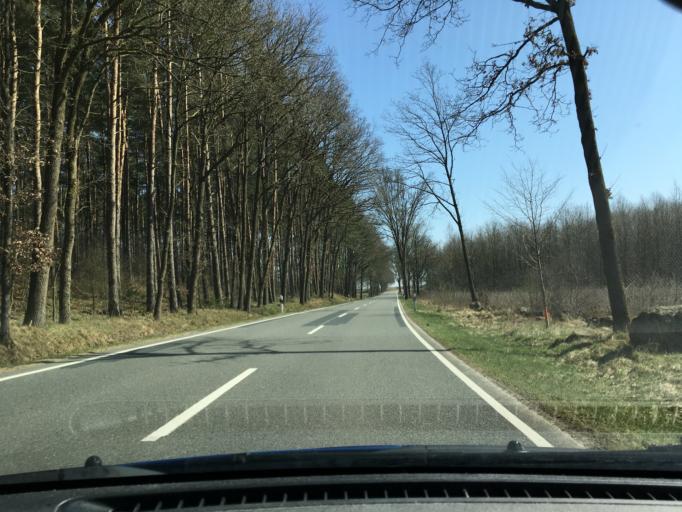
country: DE
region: Lower Saxony
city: Rehlingen
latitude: 53.1068
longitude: 10.2550
